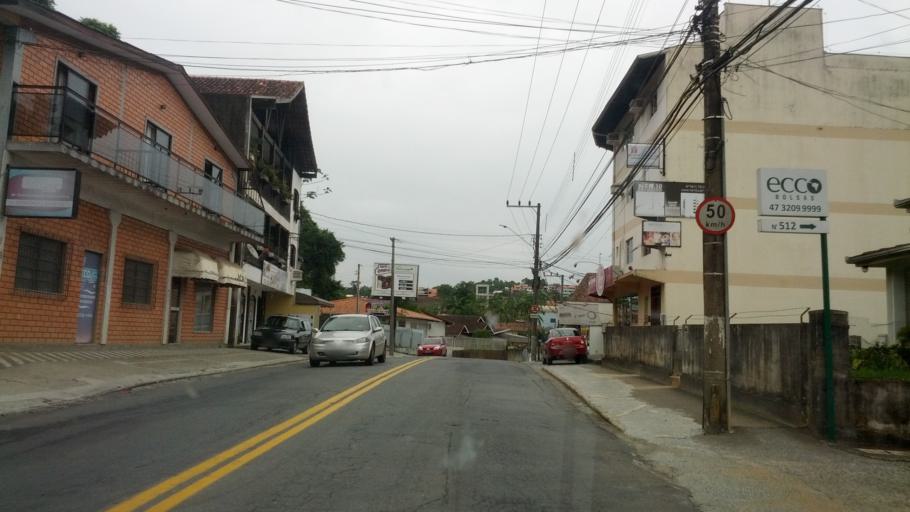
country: BR
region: Santa Catarina
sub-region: Blumenau
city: Blumenau
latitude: -26.9119
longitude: -49.0973
